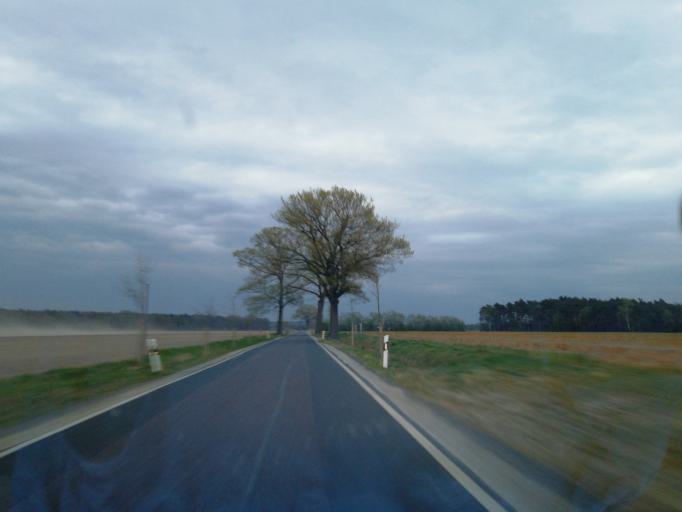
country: DE
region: Brandenburg
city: Calau
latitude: 51.7686
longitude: 13.8934
